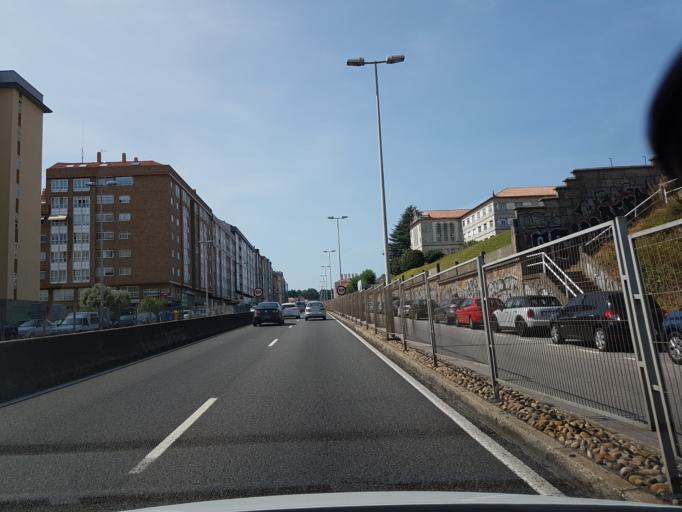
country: ES
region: Galicia
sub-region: Provincia de Pontevedra
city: Vigo
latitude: 42.2255
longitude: -8.7132
